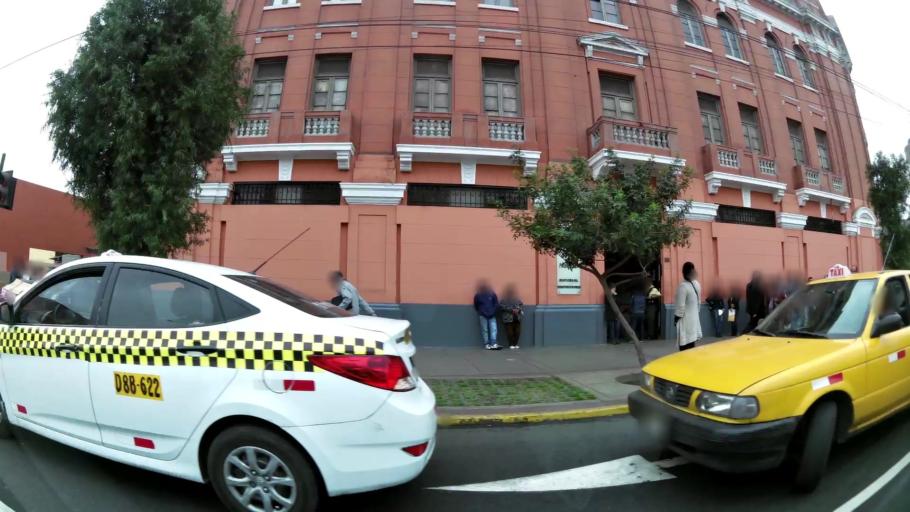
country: PE
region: Lima
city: Lima
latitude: -12.0540
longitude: -77.0373
